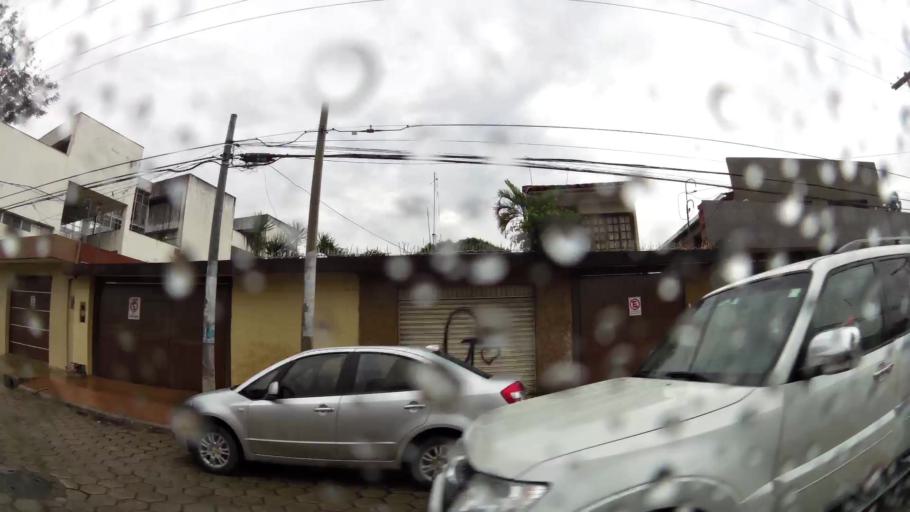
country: BO
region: Santa Cruz
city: Santa Cruz de la Sierra
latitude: -17.7766
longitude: -63.1706
